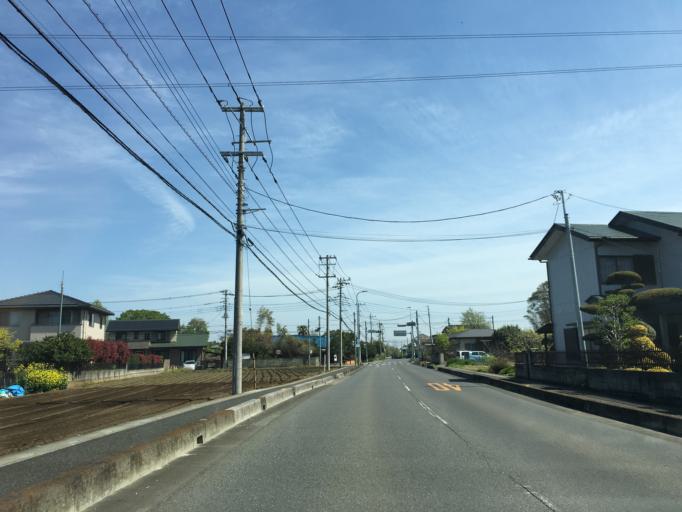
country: JP
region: Saitama
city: Sugito
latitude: 36.0089
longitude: 139.7206
